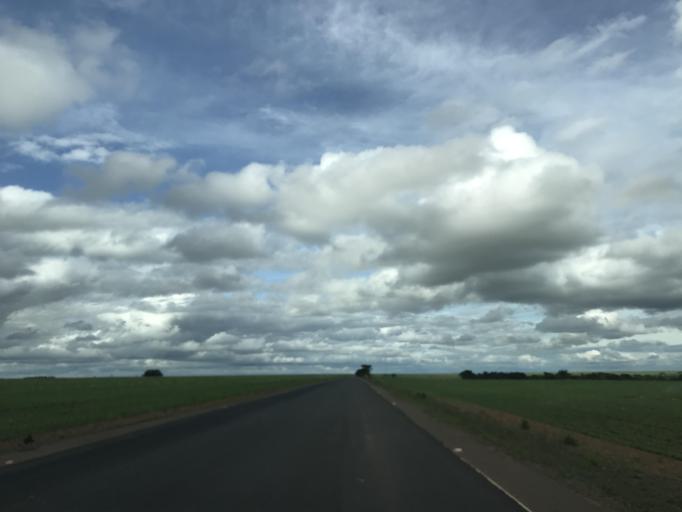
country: BR
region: Goias
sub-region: Vianopolis
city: Vianopolis
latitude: -16.9672
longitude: -48.6493
